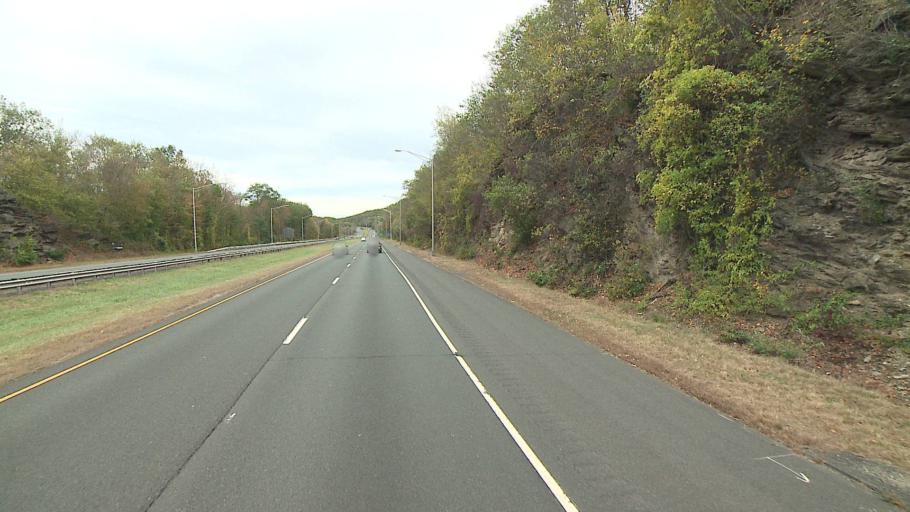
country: US
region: Connecticut
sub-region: Middlesex County
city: Higganum
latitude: 41.5218
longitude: -72.6063
